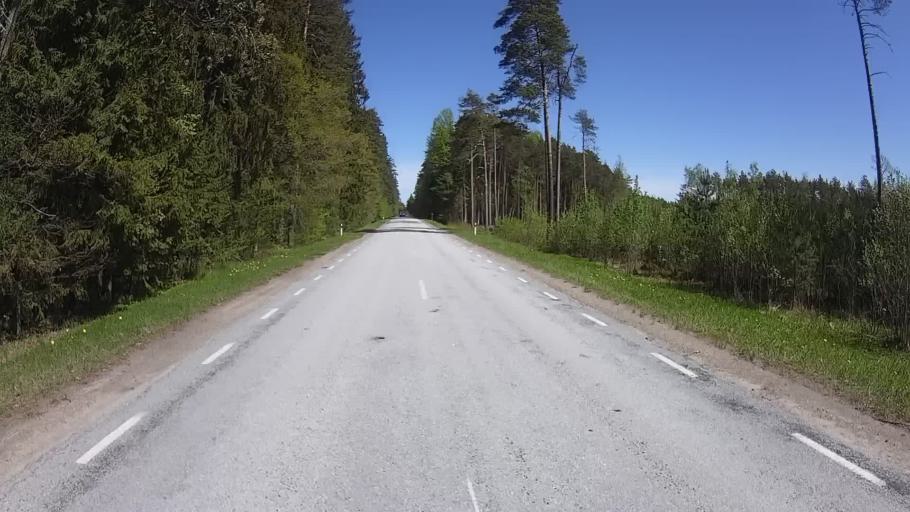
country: EE
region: Polvamaa
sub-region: Raepina vald
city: Rapina
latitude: 58.0791
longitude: 27.4288
